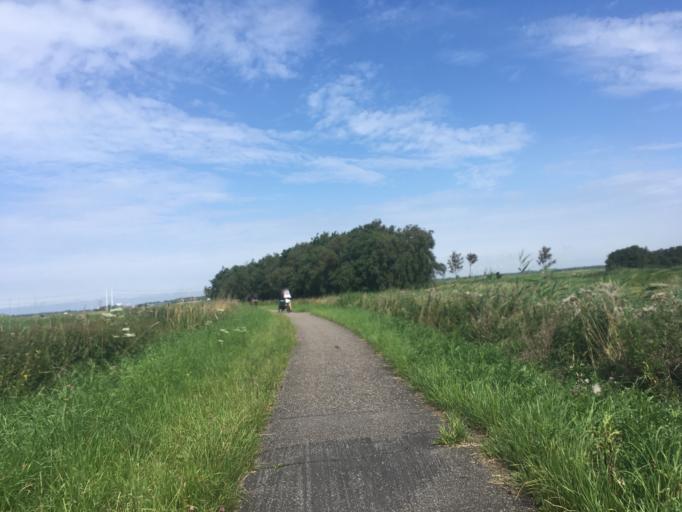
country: NL
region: North Holland
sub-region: Gemeente Haarlem
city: Haarlem
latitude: 52.4035
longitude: 4.7201
